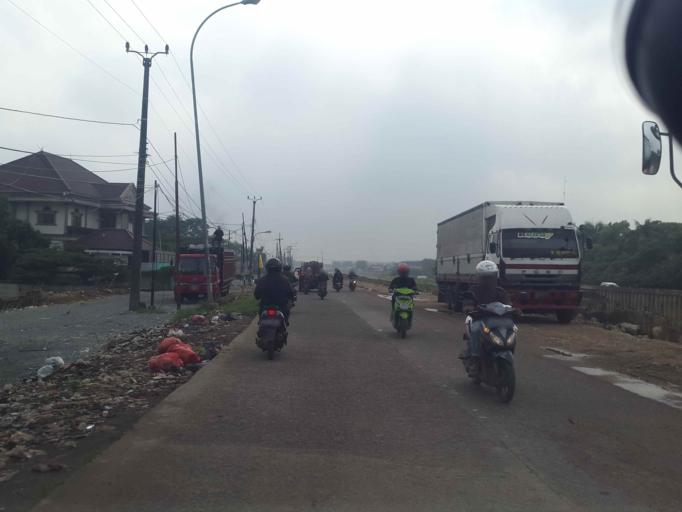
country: ID
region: West Java
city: Cikarang
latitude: -6.2820
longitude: 107.0950
